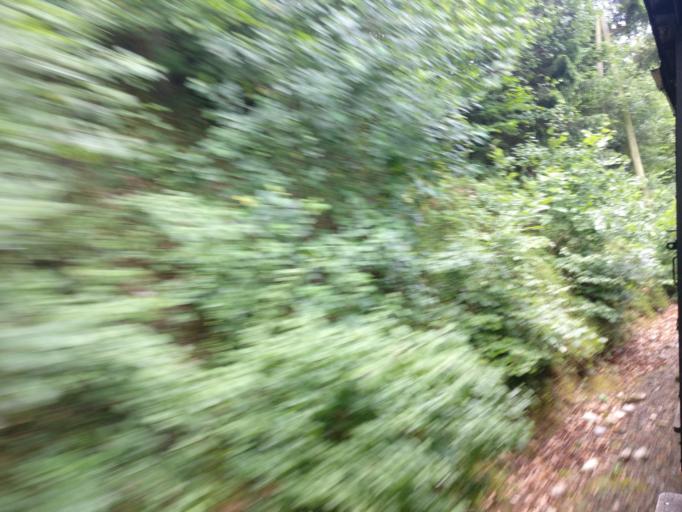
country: AT
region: Upper Austria
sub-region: Politischer Bezirk Steyr-Land
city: Waldneukirchen
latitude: 47.9968
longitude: 14.2812
